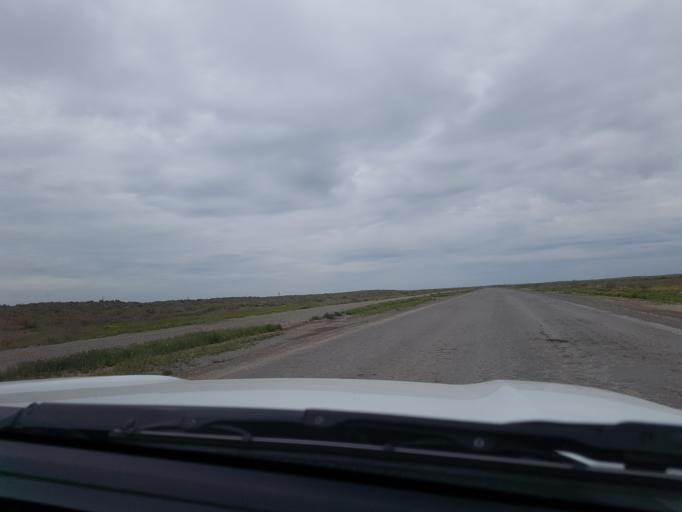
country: TM
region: Mary
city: Bayramaly
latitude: 37.9484
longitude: 62.6409
